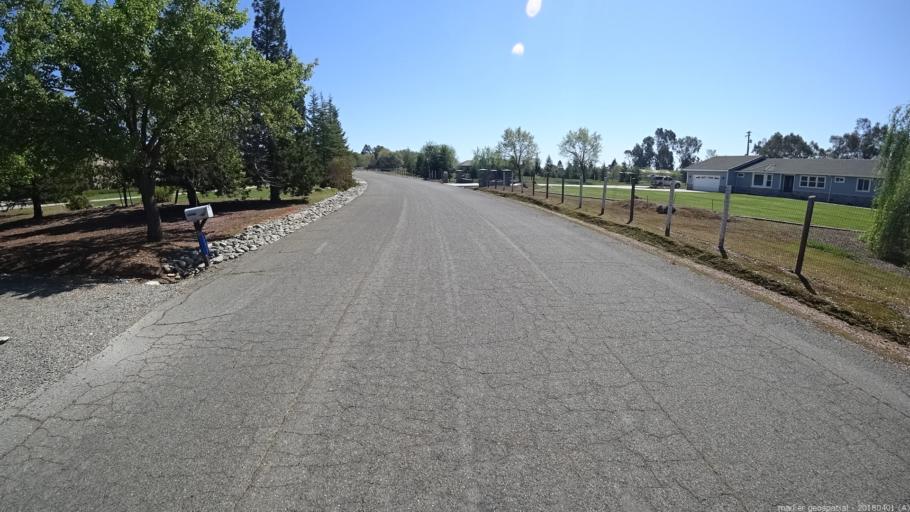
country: US
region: California
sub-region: Sacramento County
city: Wilton
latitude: 38.4119
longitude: -121.2150
